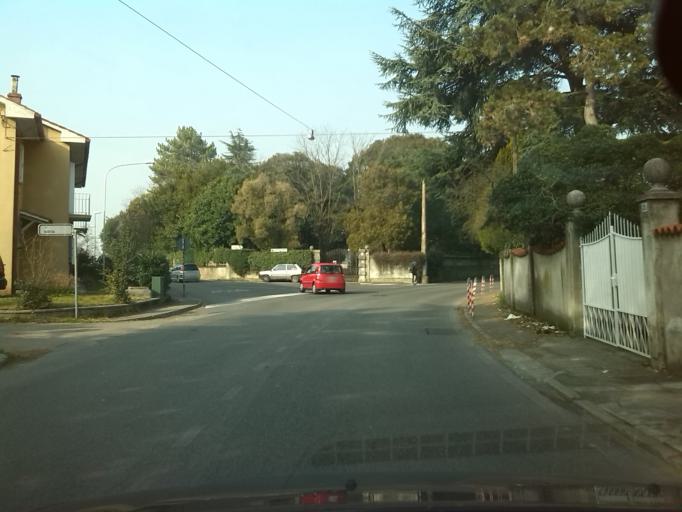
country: IT
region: Friuli Venezia Giulia
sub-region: Provincia di Gorizia
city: Gradisca d'Isonzo
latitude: 45.8939
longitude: 13.4994
